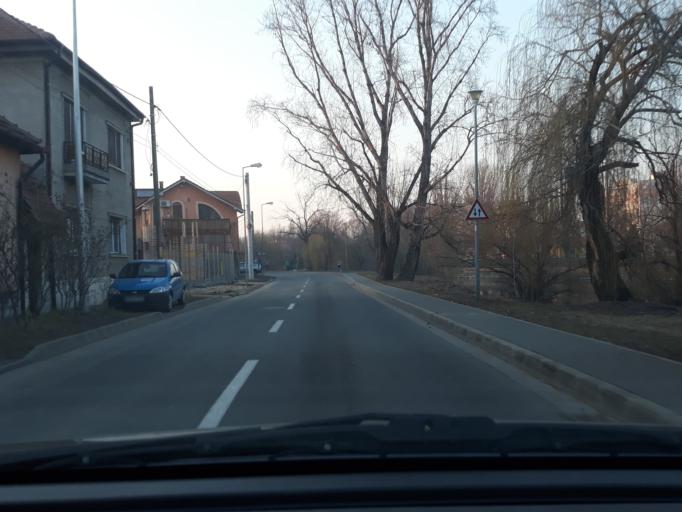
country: RO
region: Bihor
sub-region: Comuna Biharea
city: Oradea
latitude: 47.0626
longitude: 21.9246
